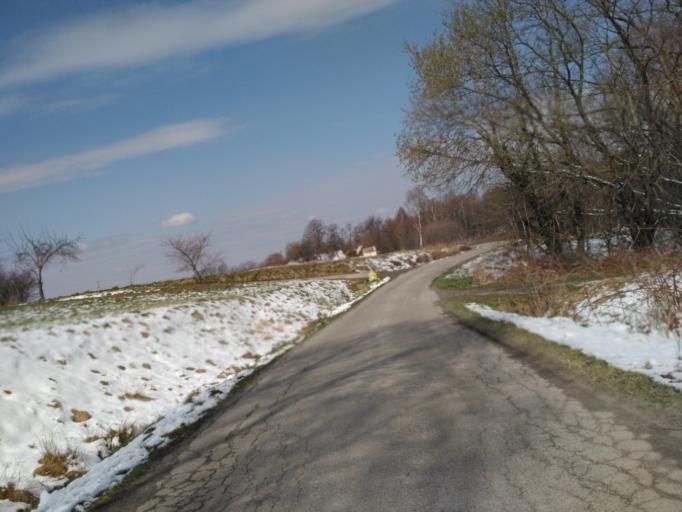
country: PL
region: Subcarpathian Voivodeship
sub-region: Powiat ropczycko-sedziszowski
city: Wielopole Skrzynskie
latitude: 49.9958
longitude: 21.5833
